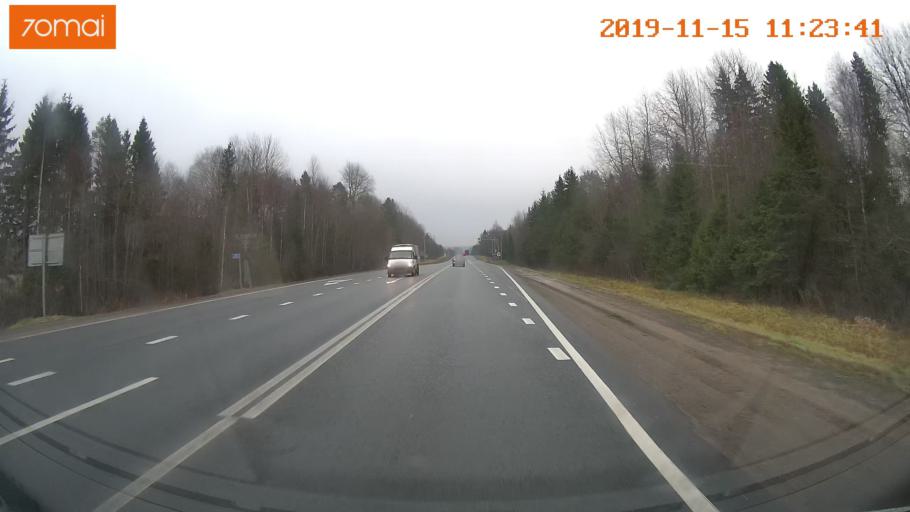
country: RU
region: Vologda
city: Molochnoye
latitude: 59.1530
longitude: 39.3881
